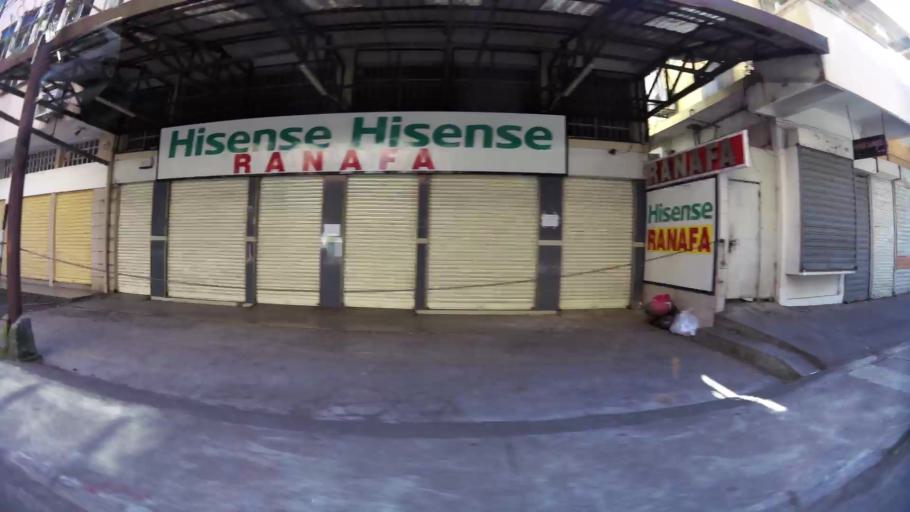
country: MU
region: Plaines Wilhems
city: Vacoas
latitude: -20.2992
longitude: 57.4919
